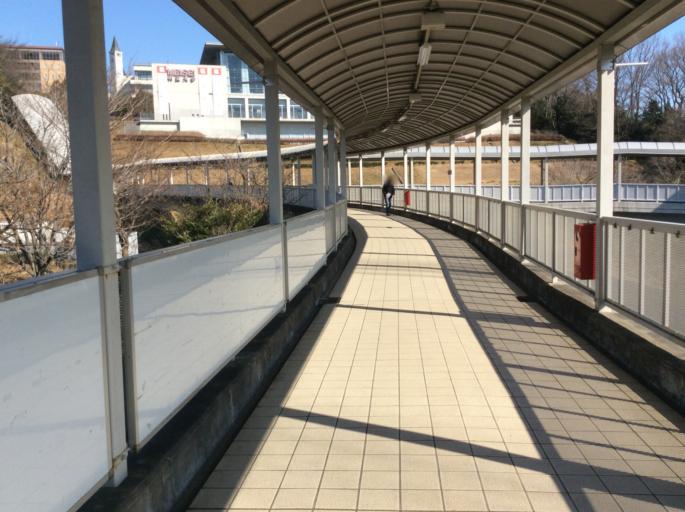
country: JP
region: Tokyo
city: Hino
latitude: 35.6422
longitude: 139.4088
